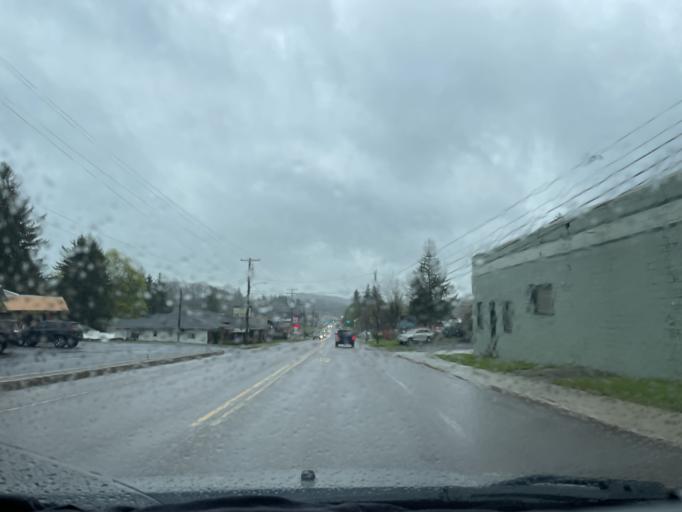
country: US
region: Maryland
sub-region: Garrett County
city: Oakland
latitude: 39.4150
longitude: -79.4031
